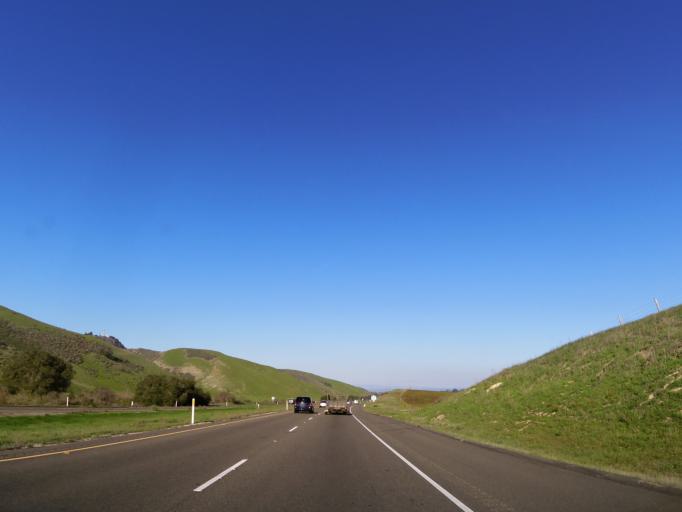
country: US
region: California
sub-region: Santa Barbara County
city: Orcutt
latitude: 34.8290
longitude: -120.3632
